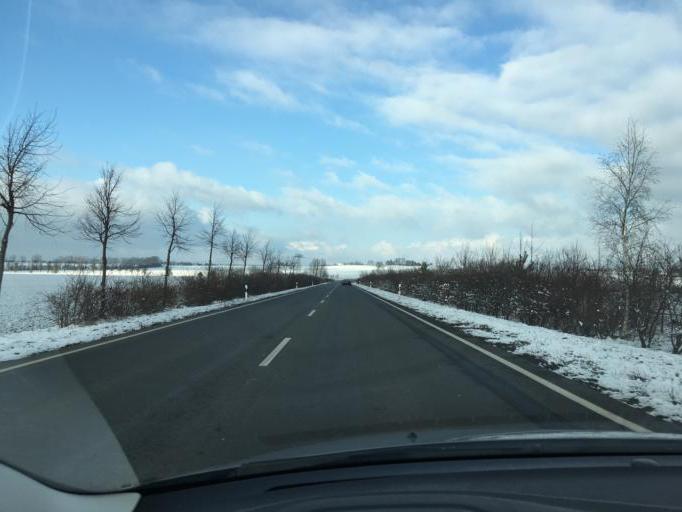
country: DE
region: Saxony
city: Grimma
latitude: 51.2373
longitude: 12.6986
